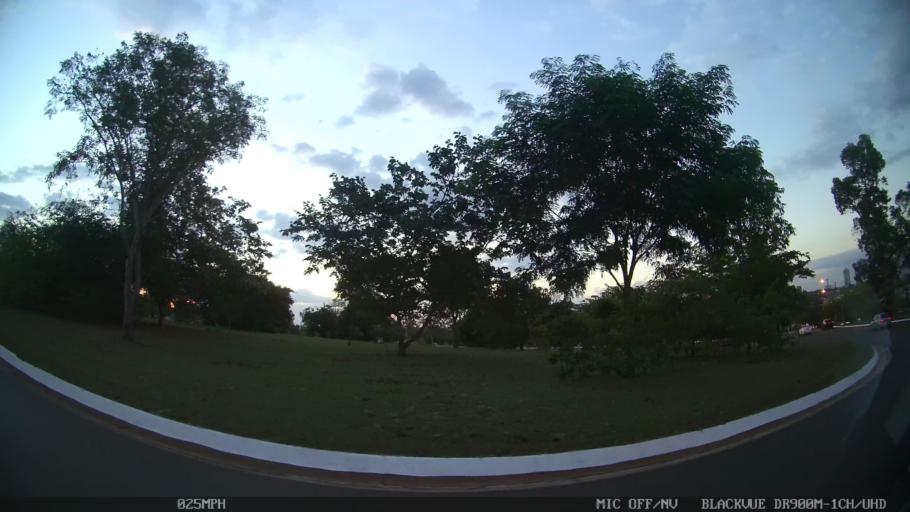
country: BR
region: Sao Paulo
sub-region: Ribeirao Preto
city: Ribeirao Preto
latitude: -21.2161
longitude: -47.7809
